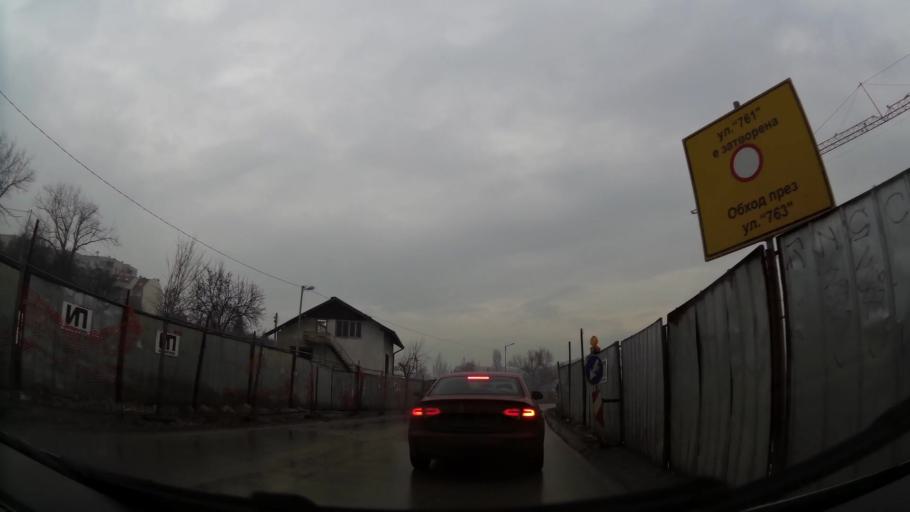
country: BG
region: Sofia-Capital
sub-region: Stolichna Obshtina
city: Sofia
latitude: 42.6836
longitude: 23.2559
